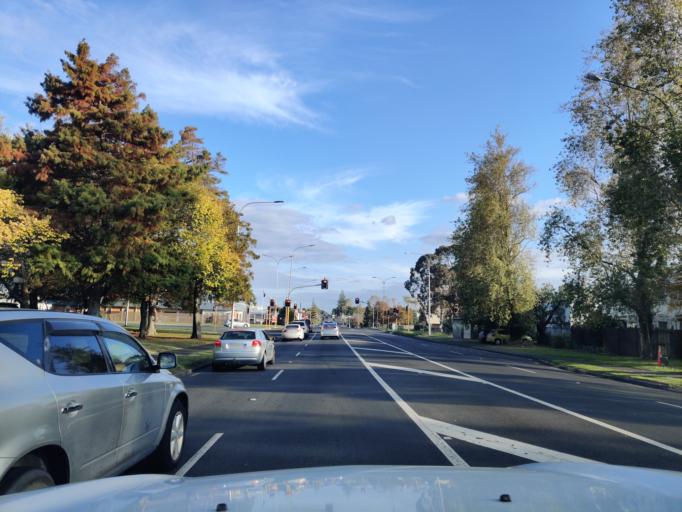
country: NZ
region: Auckland
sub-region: Auckland
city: Manukau City
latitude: -36.9532
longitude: 174.8911
